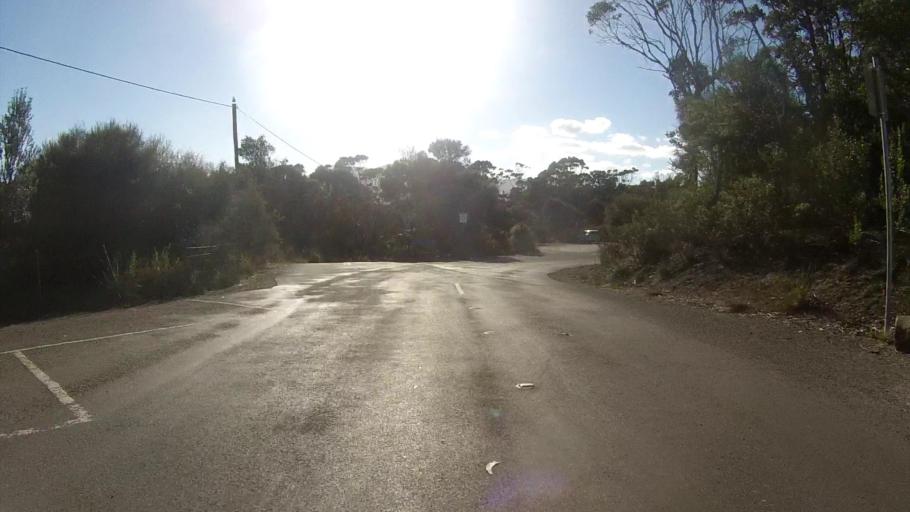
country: AU
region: Tasmania
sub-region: Clarence
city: Sandford
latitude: -43.0350
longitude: 147.9475
